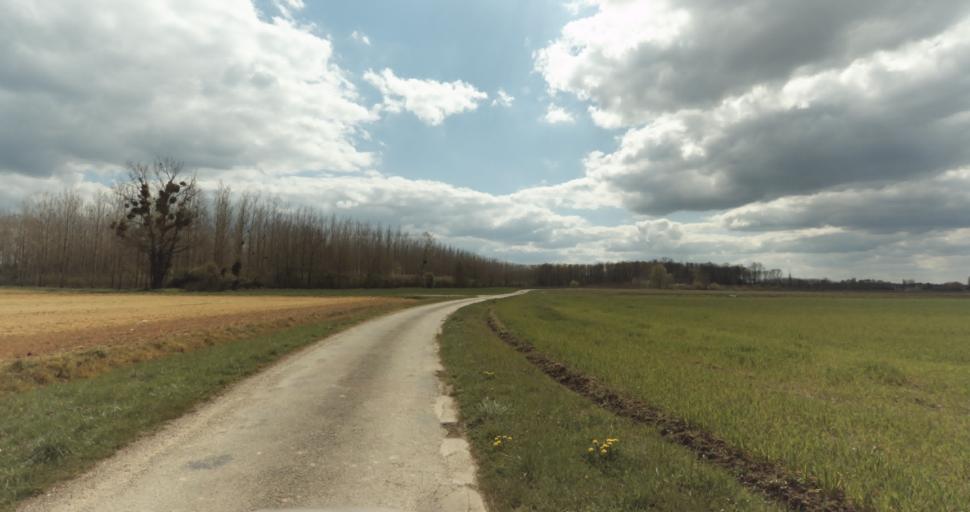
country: FR
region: Bourgogne
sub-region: Departement de la Cote-d'Or
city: Auxonne
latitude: 47.1637
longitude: 5.3963
